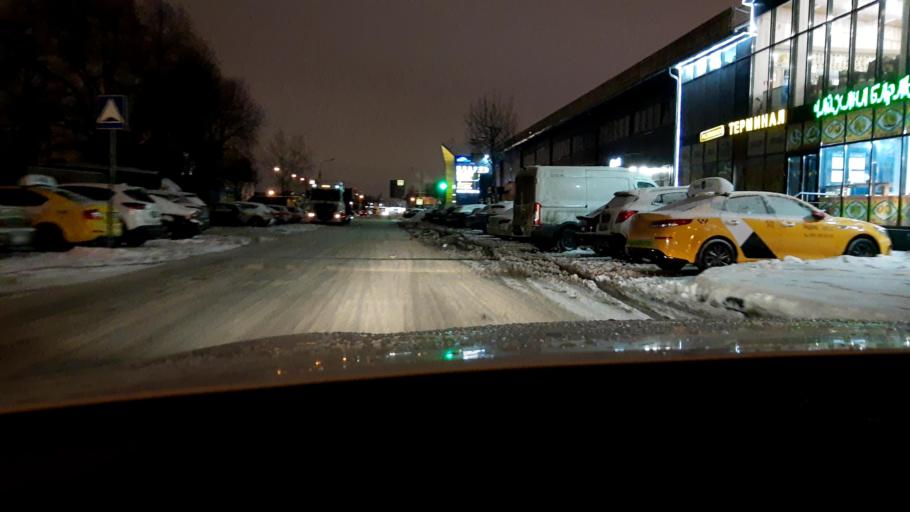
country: RU
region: Moscow
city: Khimki
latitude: 55.9148
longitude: 37.4136
